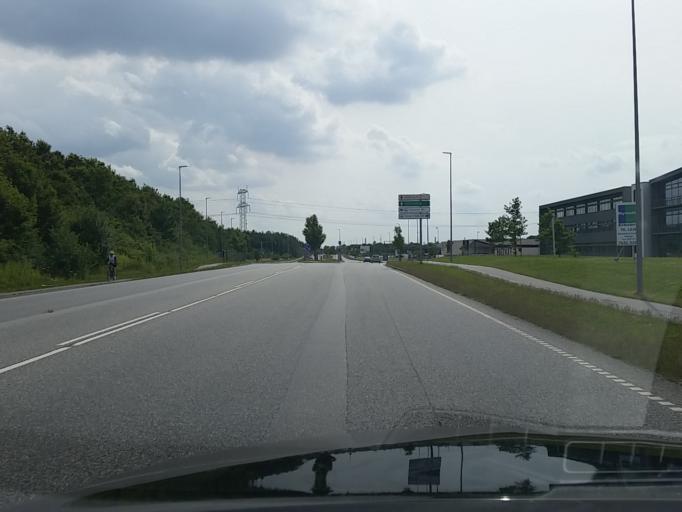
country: DK
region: South Denmark
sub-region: Kolding Kommune
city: Kolding
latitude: 55.5345
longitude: 9.4701
